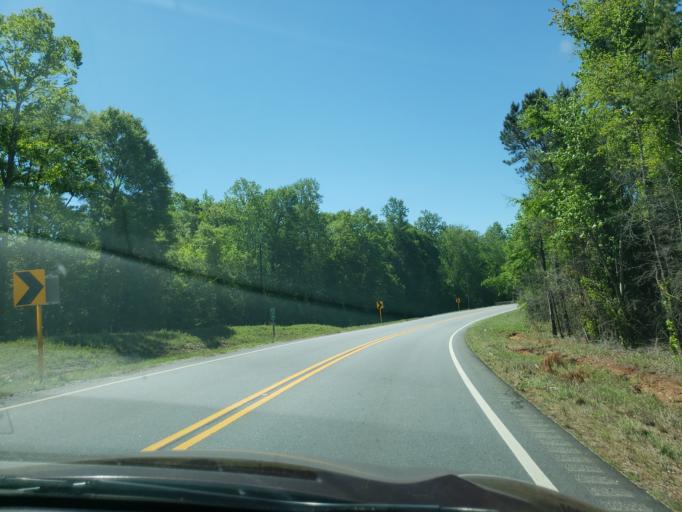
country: US
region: Alabama
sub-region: Tallapoosa County
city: Dadeville
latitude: 32.6886
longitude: -85.7837
